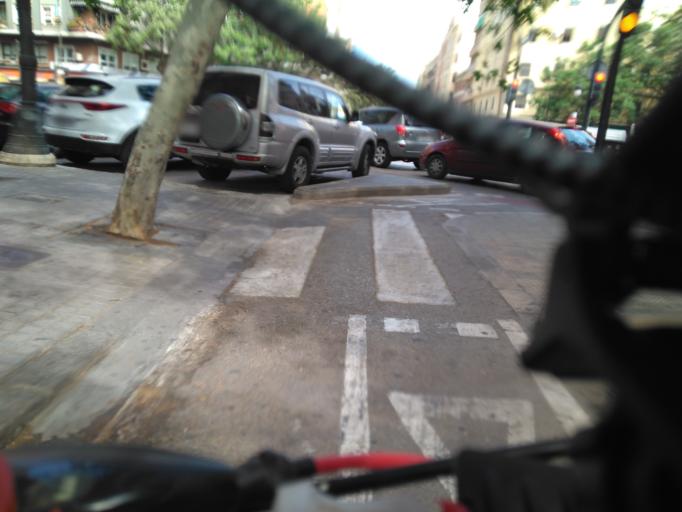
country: ES
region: Valencia
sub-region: Provincia de Valencia
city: Valencia
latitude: 39.4694
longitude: -0.3885
